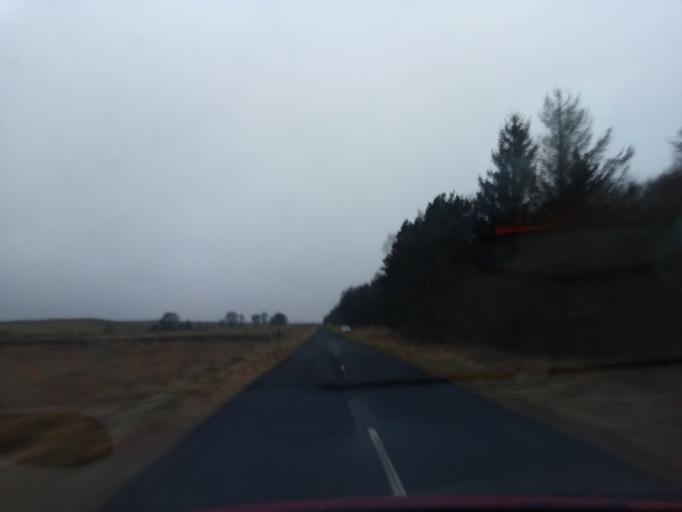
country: GB
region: England
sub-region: Northumberland
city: Rothley
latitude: 55.2080
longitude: -2.0370
